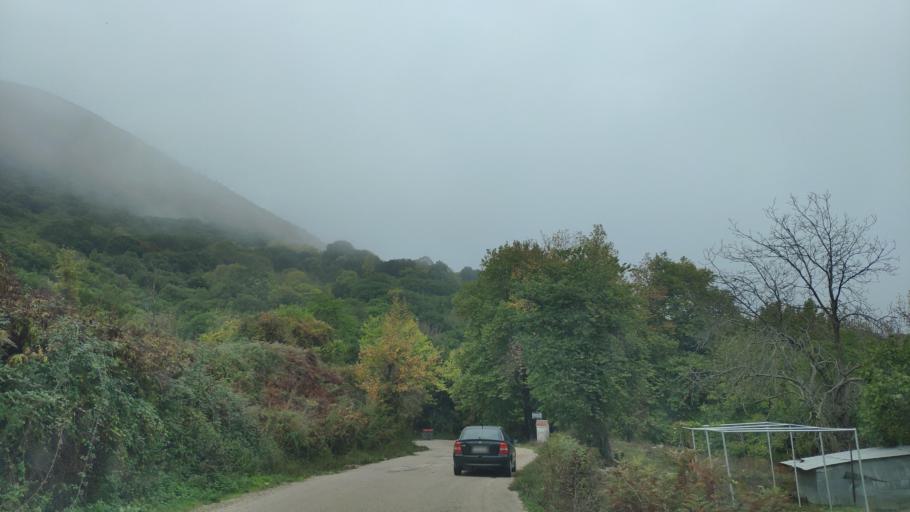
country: GR
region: Epirus
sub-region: Nomos Thesprotias
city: Paramythia
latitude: 39.4717
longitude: 20.6693
